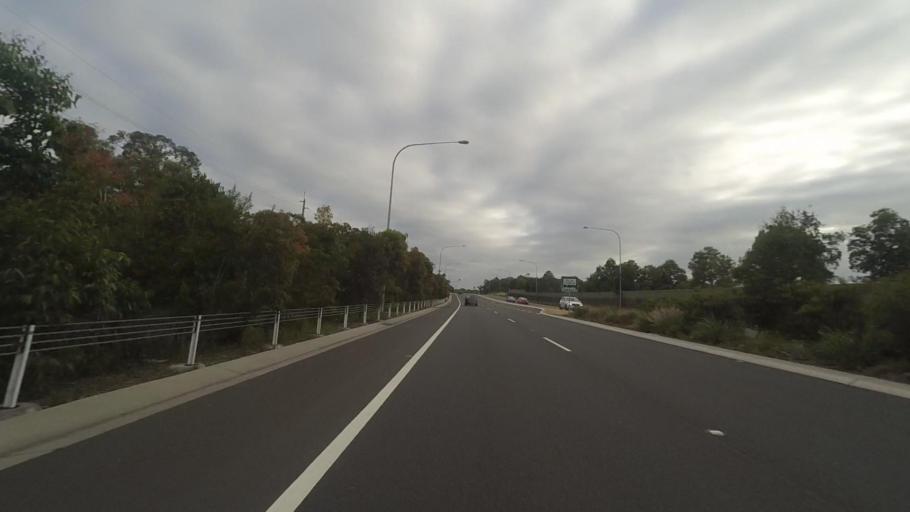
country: AU
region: New South Wales
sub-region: Sutherland Shire
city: Menai
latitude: -34.0267
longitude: 151.0071
